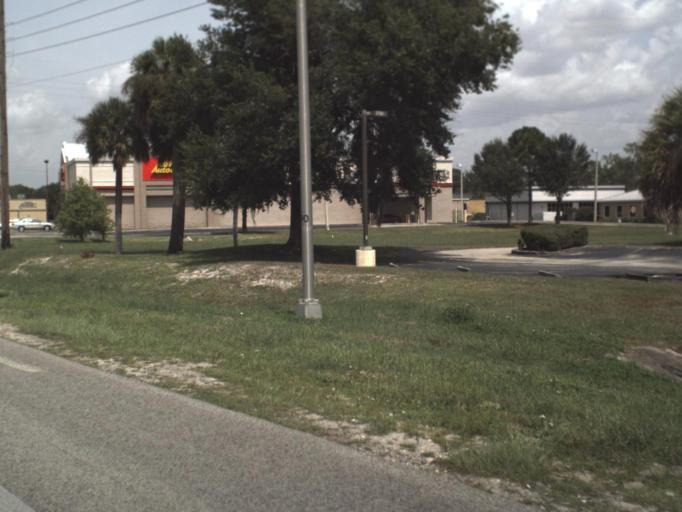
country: US
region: Florida
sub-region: Highlands County
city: Sebring
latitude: 27.5133
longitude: -81.4943
